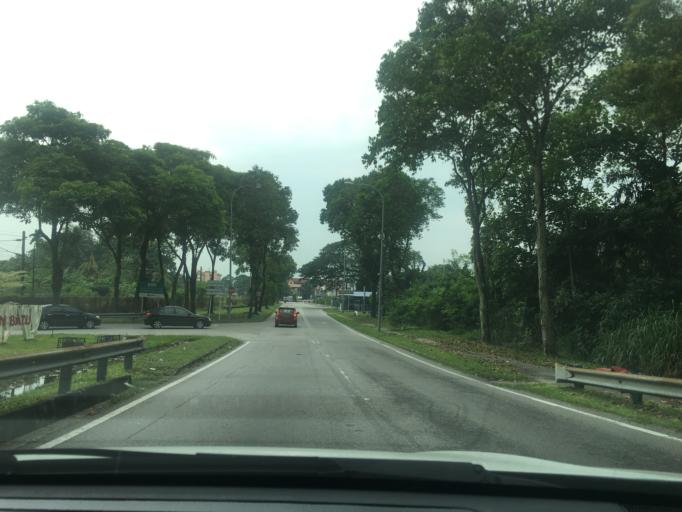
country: MY
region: Selangor
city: Klang
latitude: 3.0472
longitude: 101.4416
